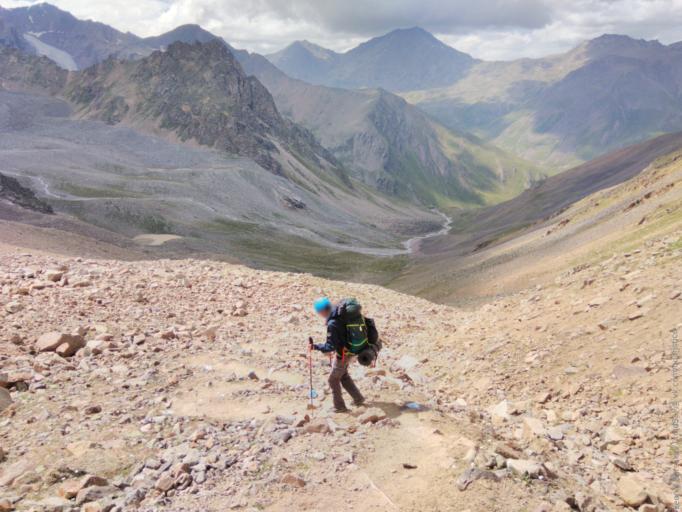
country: RU
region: Kabardino-Balkariya
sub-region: El'brusskiy Rayon
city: El'brus
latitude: 43.3369
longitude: 42.6621
